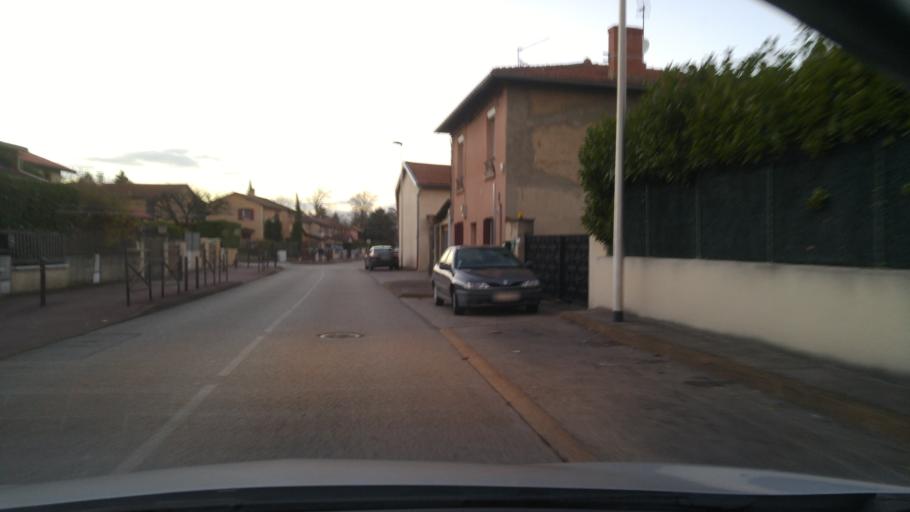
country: FR
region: Rhone-Alpes
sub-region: Departement du Rhone
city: Saint-Laurent-de-Mure
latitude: 45.6910
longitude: 5.0332
